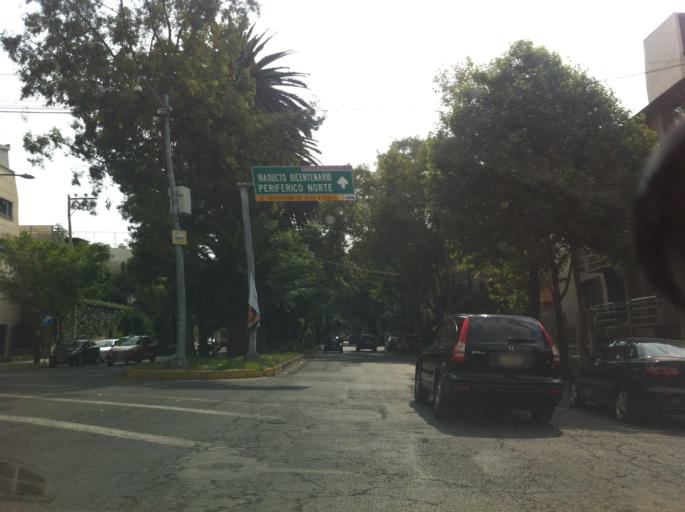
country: MX
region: Mexico City
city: Miguel Hidalgo
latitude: 19.4328
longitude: -99.1754
